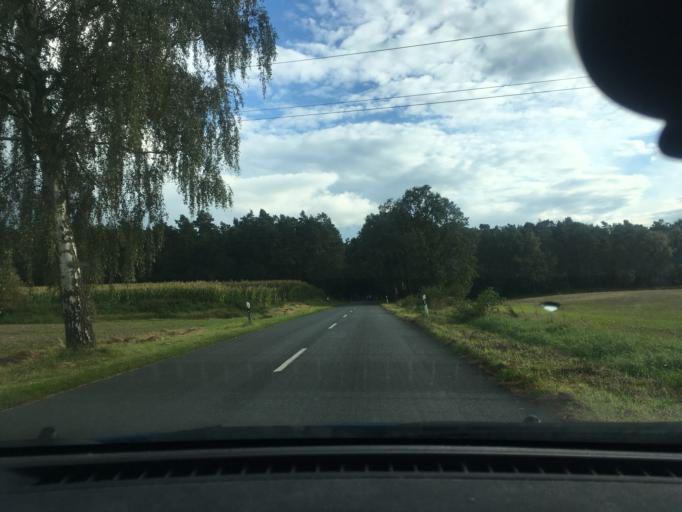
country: DE
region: Lower Saxony
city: Gohrde
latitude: 53.1575
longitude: 10.8672
